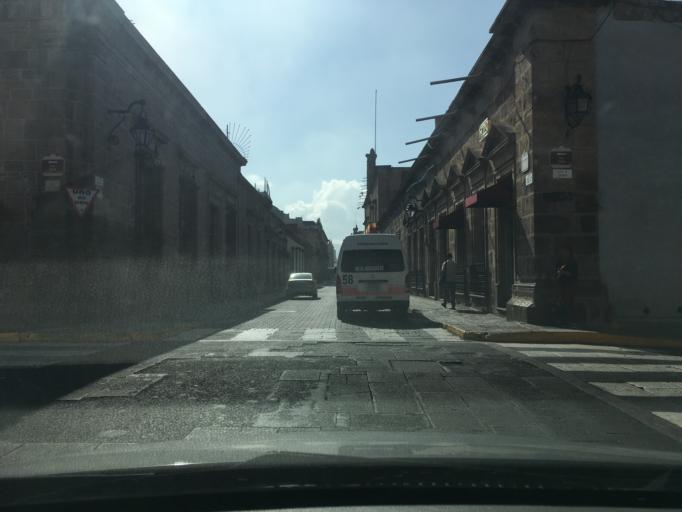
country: MX
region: Michoacan
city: Morelia
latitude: 19.7019
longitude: -101.1960
